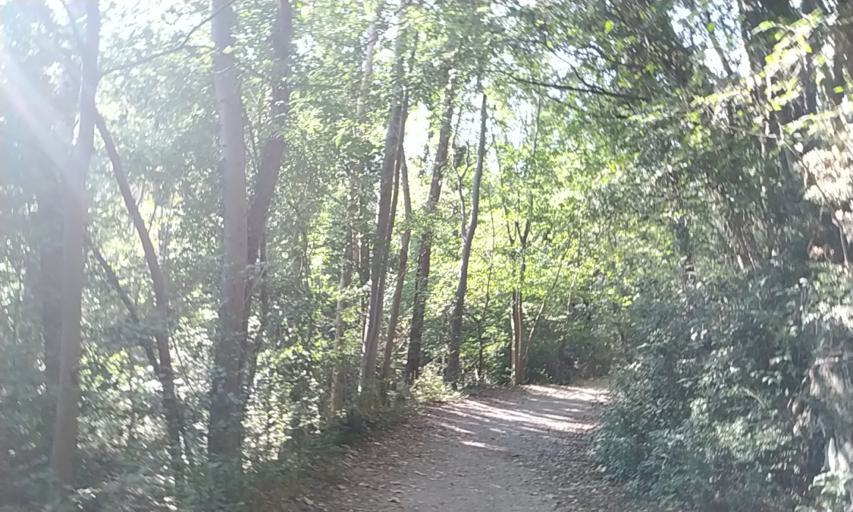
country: IT
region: Piedmont
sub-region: Provincia di Torino
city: Chiaverano
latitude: 45.4925
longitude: 7.8869
